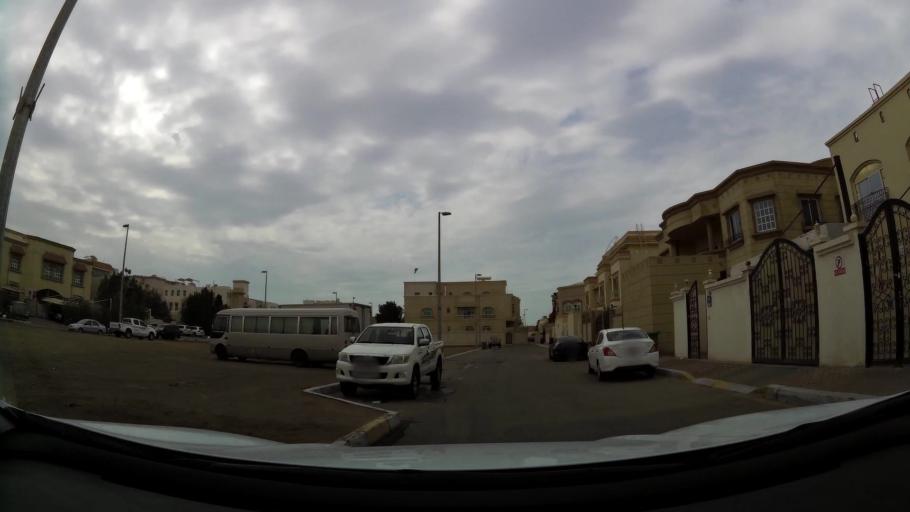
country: AE
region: Abu Dhabi
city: Abu Dhabi
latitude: 24.4322
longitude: 54.4118
